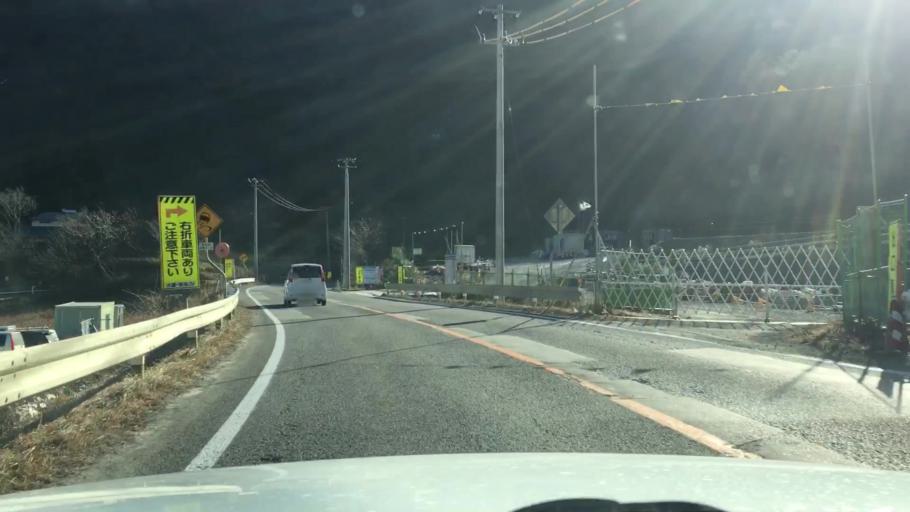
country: JP
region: Iwate
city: Miyako
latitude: 39.5994
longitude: 141.7609
